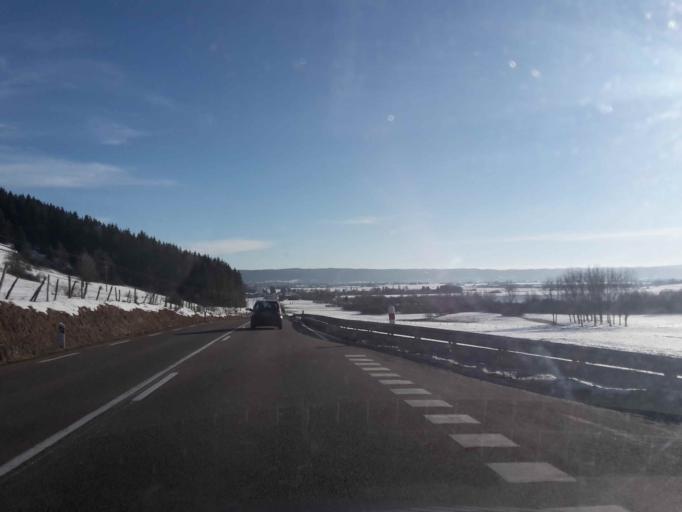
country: FR
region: Franche-Comte
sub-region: Departement du Doubs
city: Doubs
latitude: 46.9572
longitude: 6.3415
